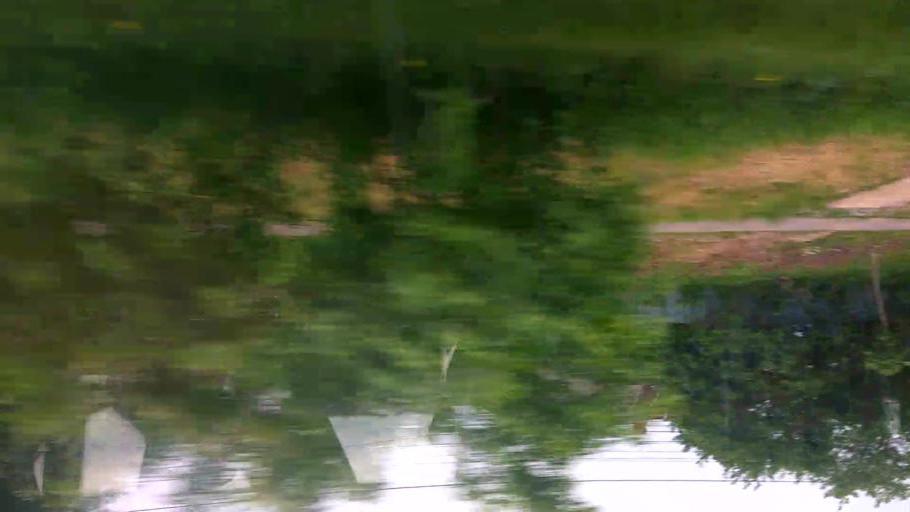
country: RU
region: Moskovskaya
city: Lukhovitsy
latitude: 54.9377
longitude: 39.0134
